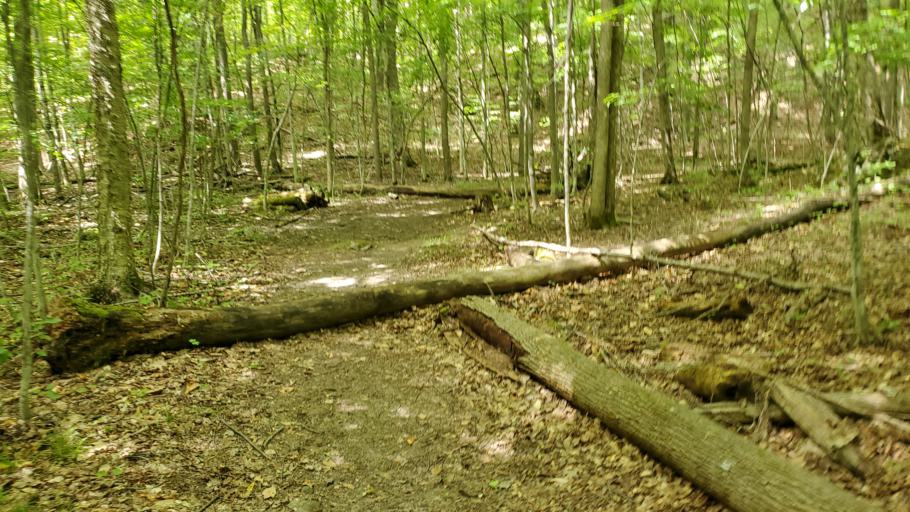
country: CA
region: Ontario
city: Gananoque
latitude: 44.5496
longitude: -76.3673
